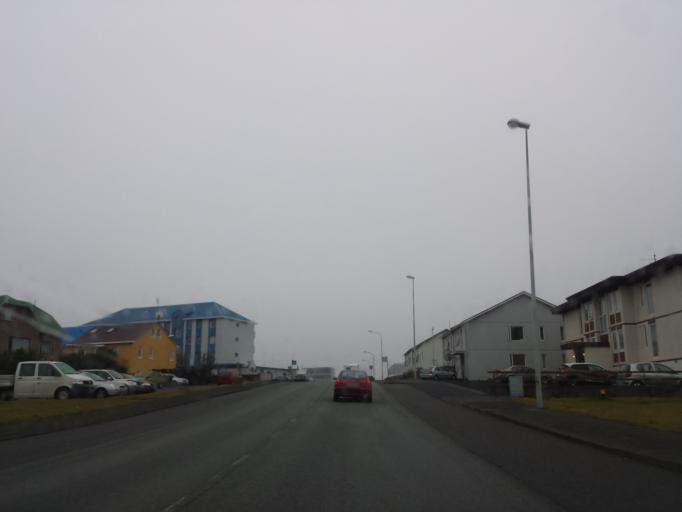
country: IS
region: Southern Peninsula
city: Reykjanesbaer
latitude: 63.9982
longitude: -22.5563
